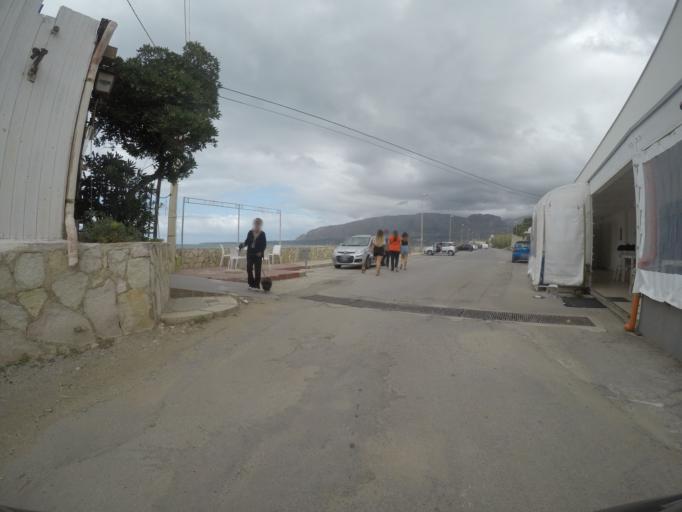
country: IT
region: Sicily
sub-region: Palermo
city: Trappeto
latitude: 38.0728
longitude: 13.0543
